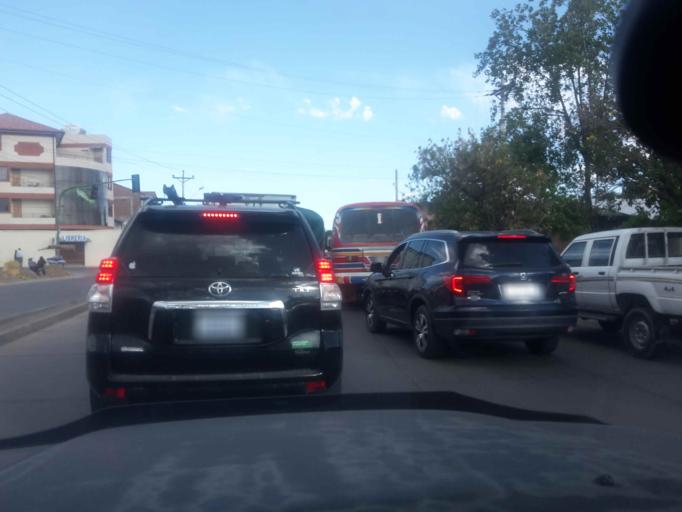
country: BO
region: Cochabamba
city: Cochabamba
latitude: -17.3520
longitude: -66.1830
